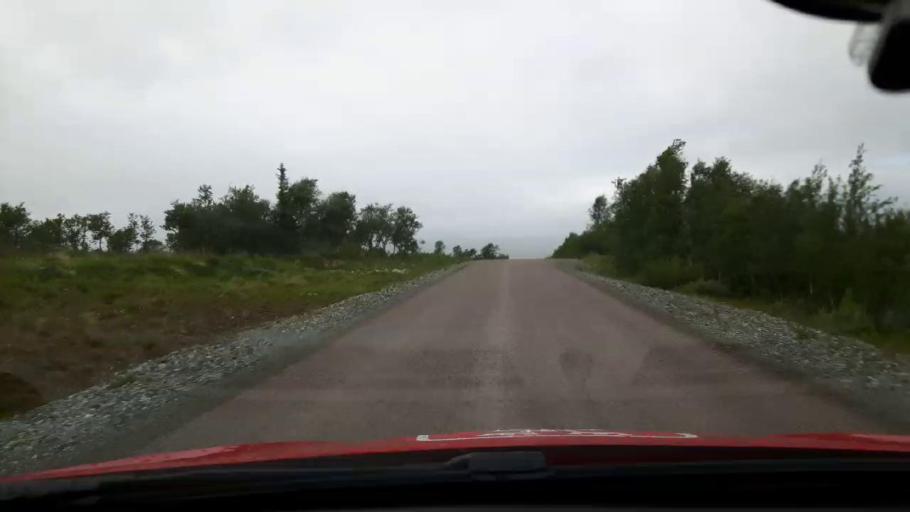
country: SE
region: Jaemtland
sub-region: Are Kommun
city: Are
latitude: 63.2394
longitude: 12.4305
